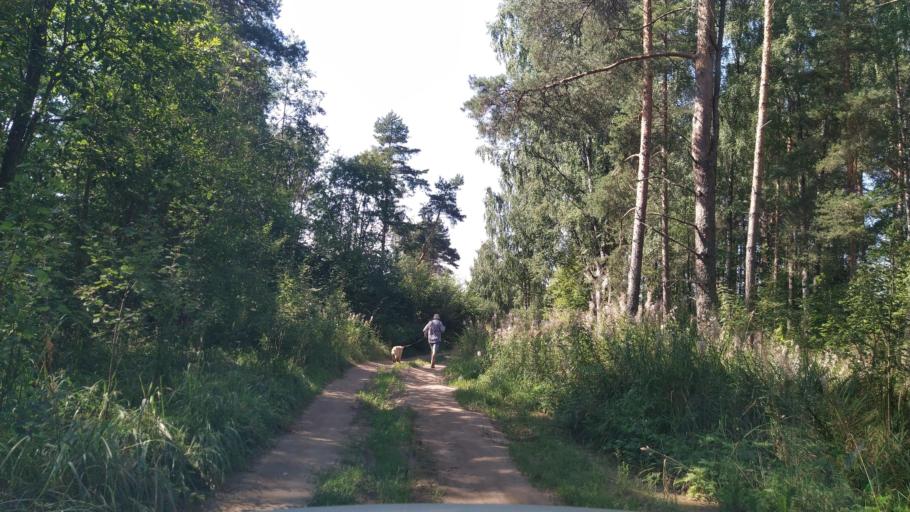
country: RU
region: Leningrad
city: Druzhnaya Gorka
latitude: 59.2674
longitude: 30.0523
